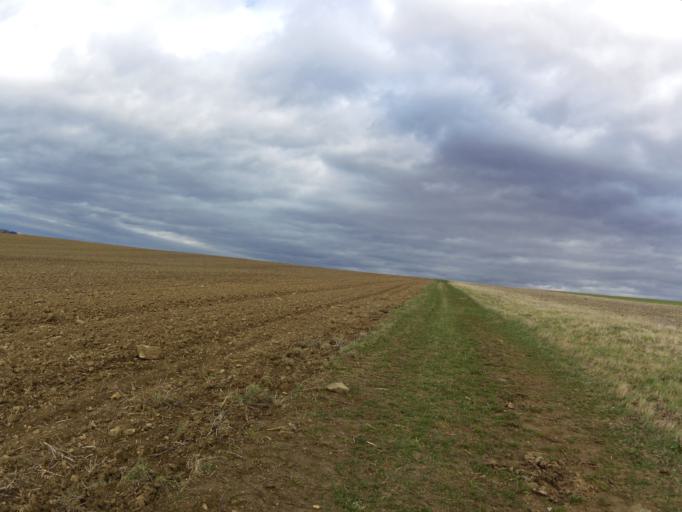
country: DE
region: Bavaria
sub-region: Regierungsbezirk Unterfranken
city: Estenfeld
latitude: 49.8127
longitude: 10.0075
